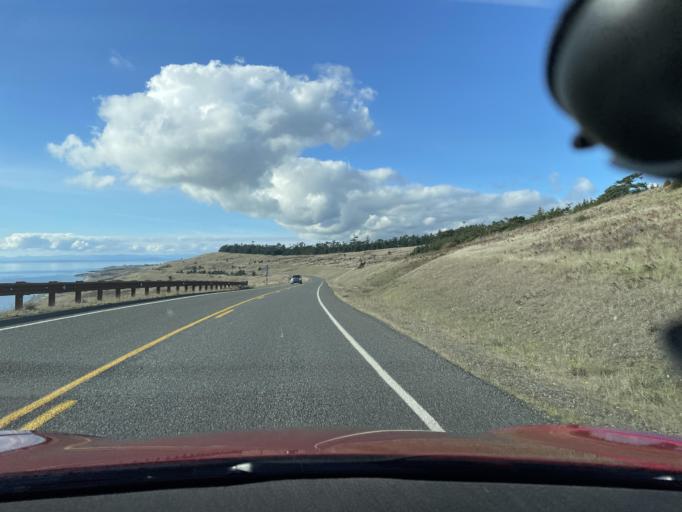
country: US
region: Washington
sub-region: San Juan County
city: Friday Harbor
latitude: 48.4552
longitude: -122.9761
